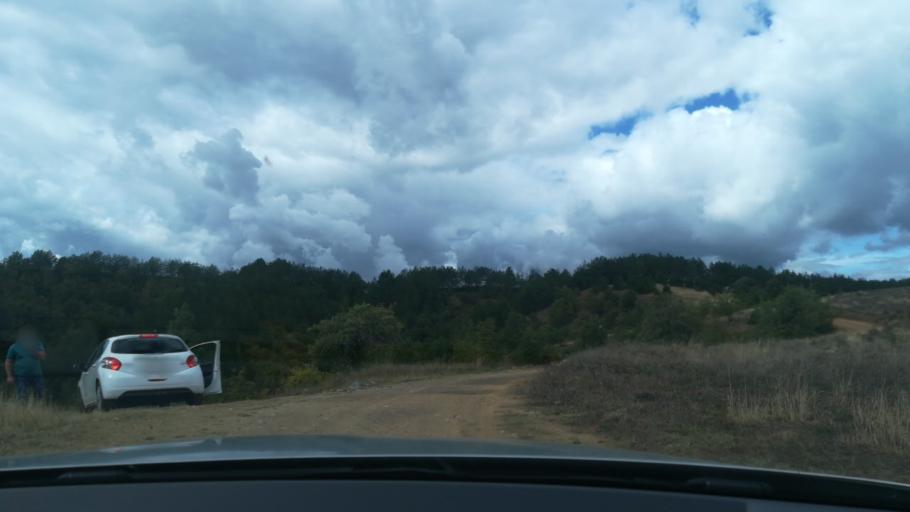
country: MK
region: Makedonska Kamenica
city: Makedonska Kamenica
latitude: 42.0054
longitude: 22.6079
